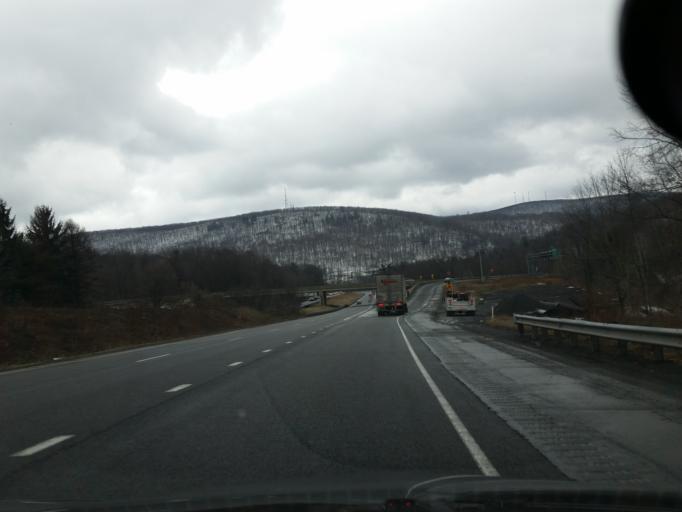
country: US
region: Pennsylvania
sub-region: Lackawanna County
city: Chinchilla
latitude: 41.4845
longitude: -75.6792
